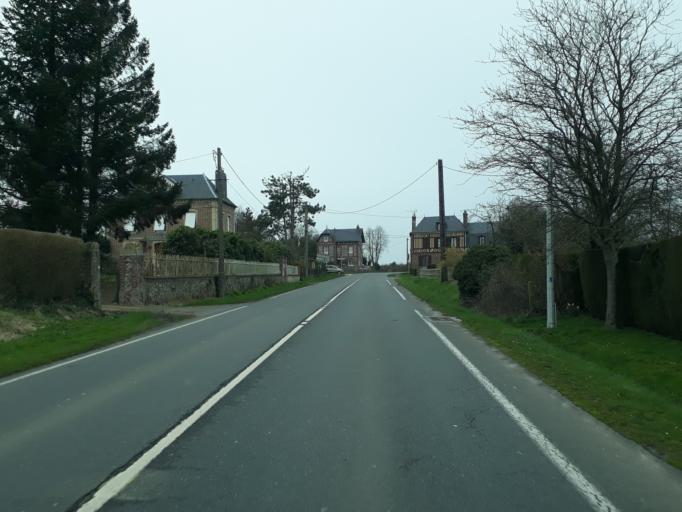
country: FR
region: Haute-Normandie
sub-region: Departement de la Seine-Maritime
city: Beuzeville-la-Grenier
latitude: 49.5953
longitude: 0.4223
